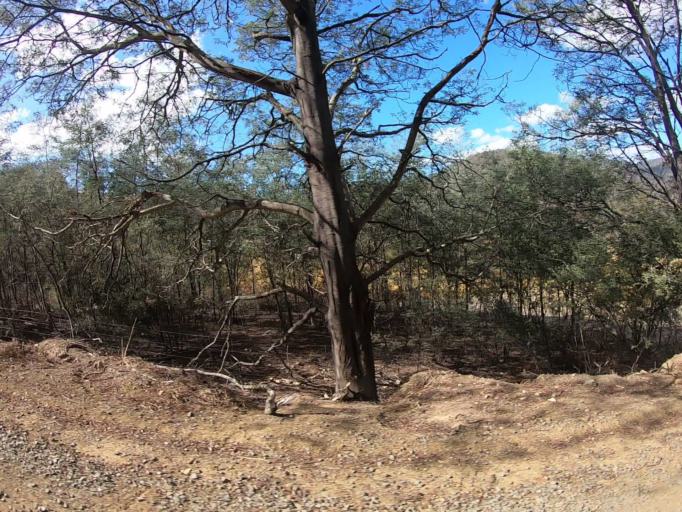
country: AU
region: Tasmania
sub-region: Brighton
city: Bridgewater
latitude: -42.4991
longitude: 147.4270
